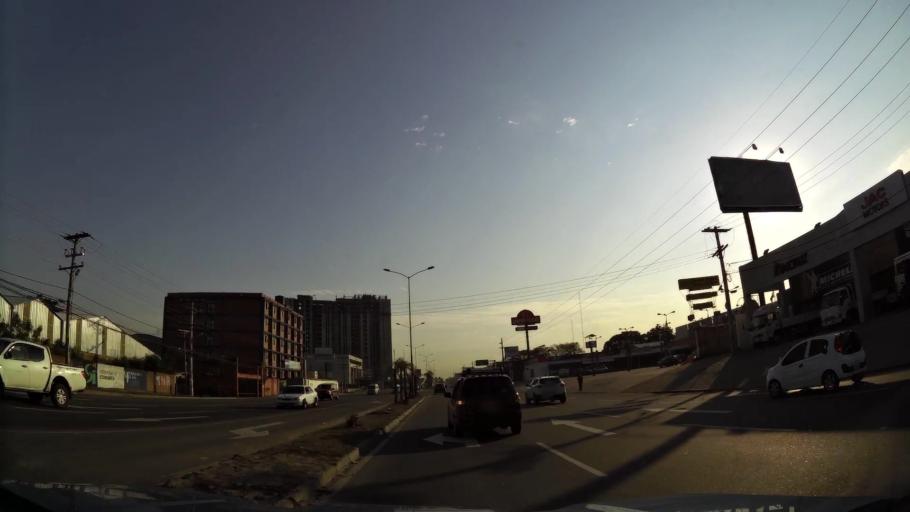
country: BO
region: Santa Cruz
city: Santa Cruz de la Sierra
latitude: -17.7291
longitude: -63.1671
